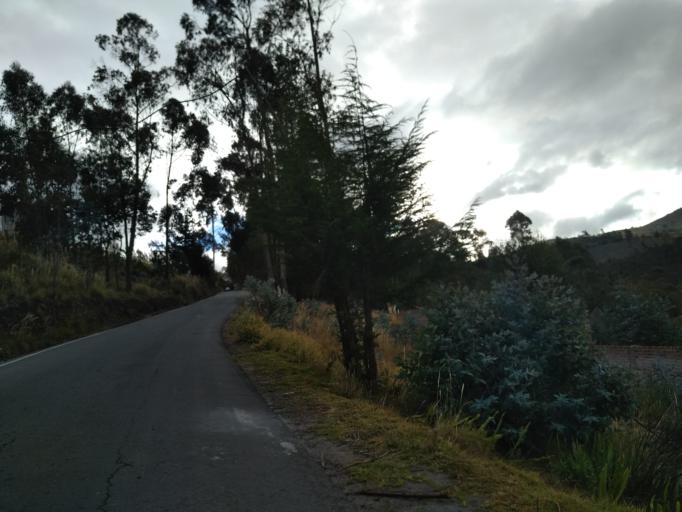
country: EC
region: Chimborazo
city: Riobamba
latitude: -1.7049
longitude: -78.6996
